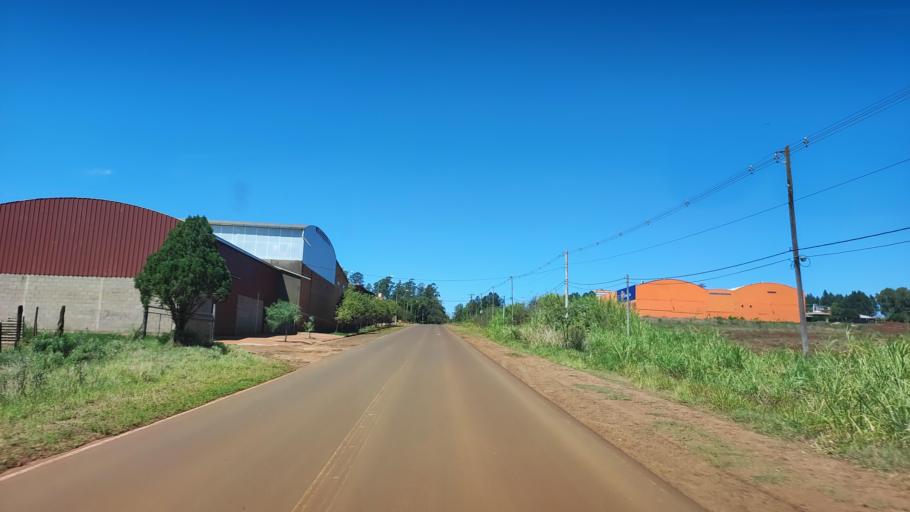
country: AR
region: Misiones
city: Puerto Rico
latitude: -26.8176
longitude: -55.0078
